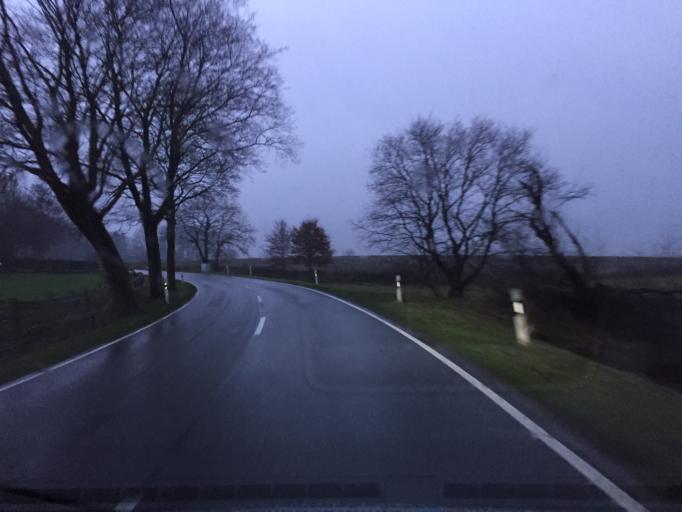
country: DE
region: Lower Saxony
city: Sudwalde
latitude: 52.8472
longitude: 8.8447
